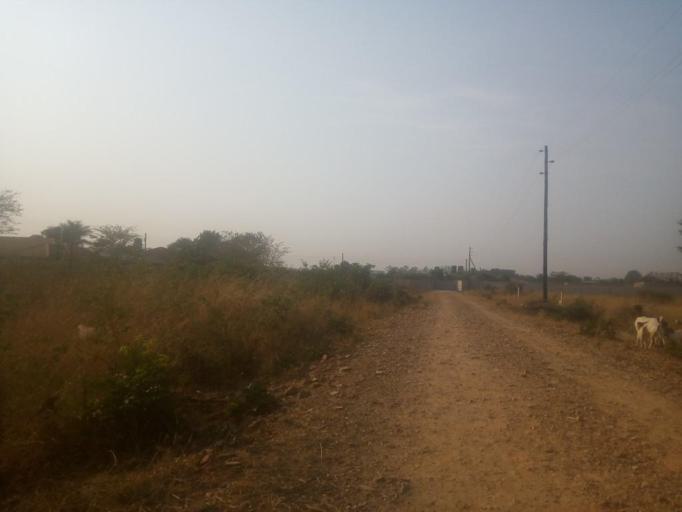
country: ZM
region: Lusaka
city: Lusaka
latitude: -15.4003
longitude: 28.3846
